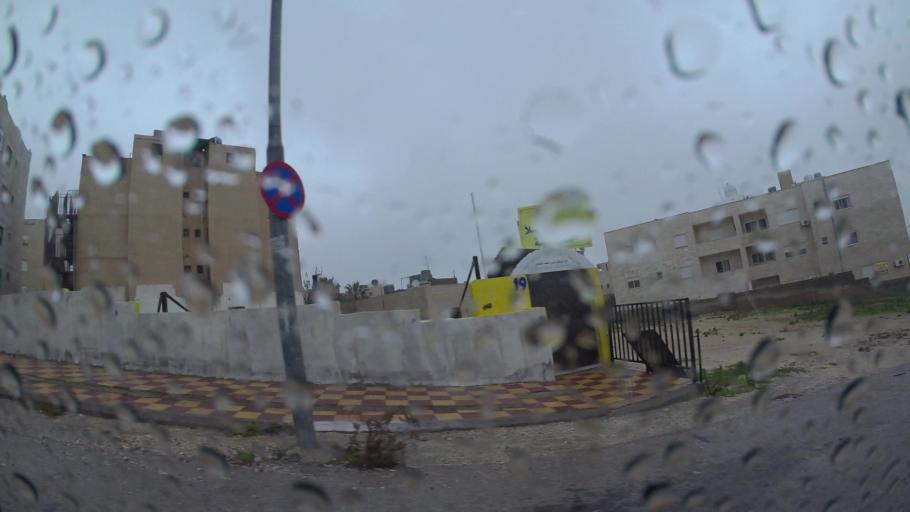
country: JO
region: Amman
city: Al Jubayhah
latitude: 32.0462
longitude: 35.8752
